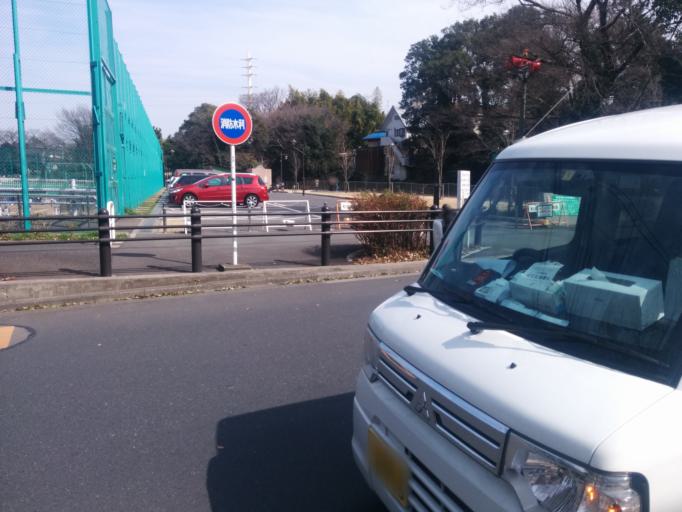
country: JP
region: Tokyo
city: Tokyo
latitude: 35.6835
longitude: 139.6424
